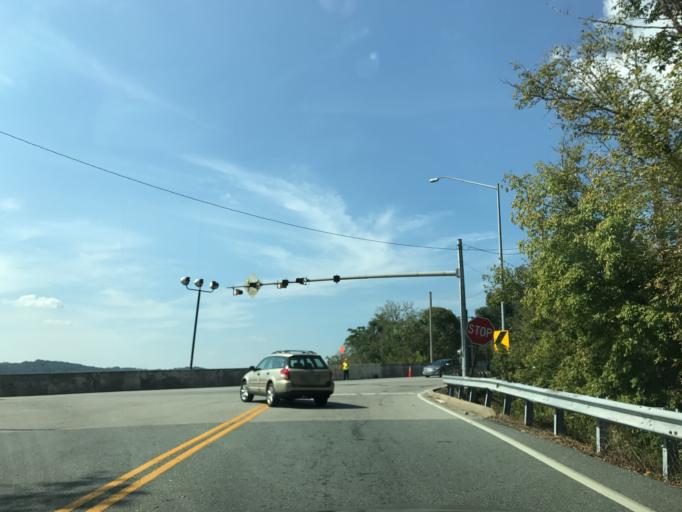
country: US
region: Maryland
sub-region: Cecil County
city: Rising Sun
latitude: 39.6676
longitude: -76.1695
